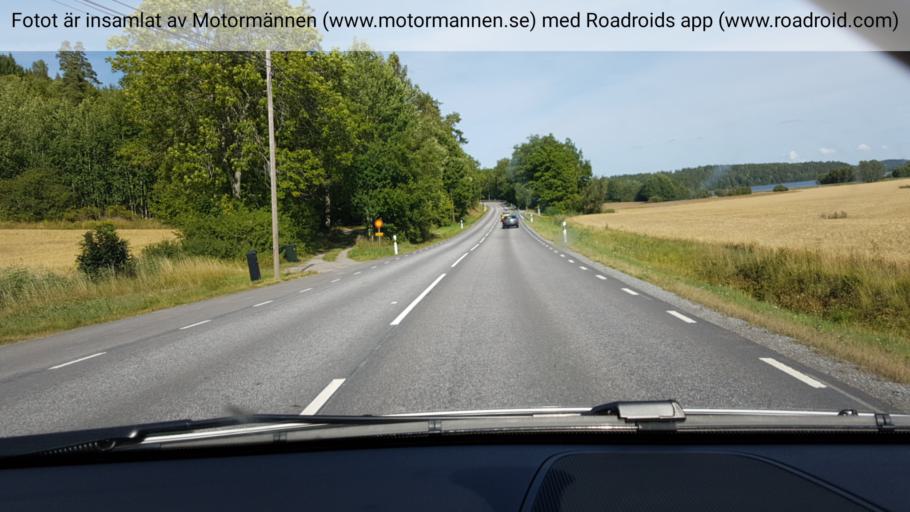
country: SE
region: Stockholm
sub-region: Sodertalje Kommun
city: Pershagen
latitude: 59.1014
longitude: 17.6275
